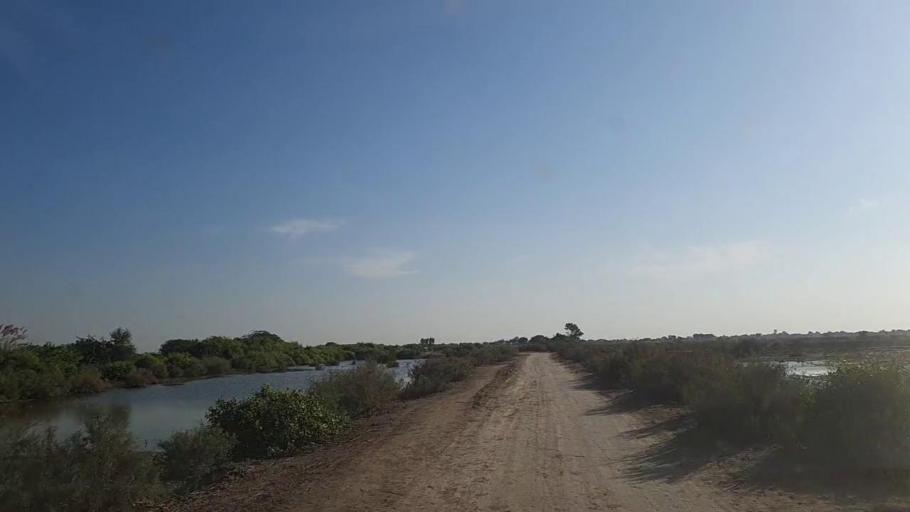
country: PK
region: Sindh
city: Mirpur Batoro
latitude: 24.7583
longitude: 68.3642
